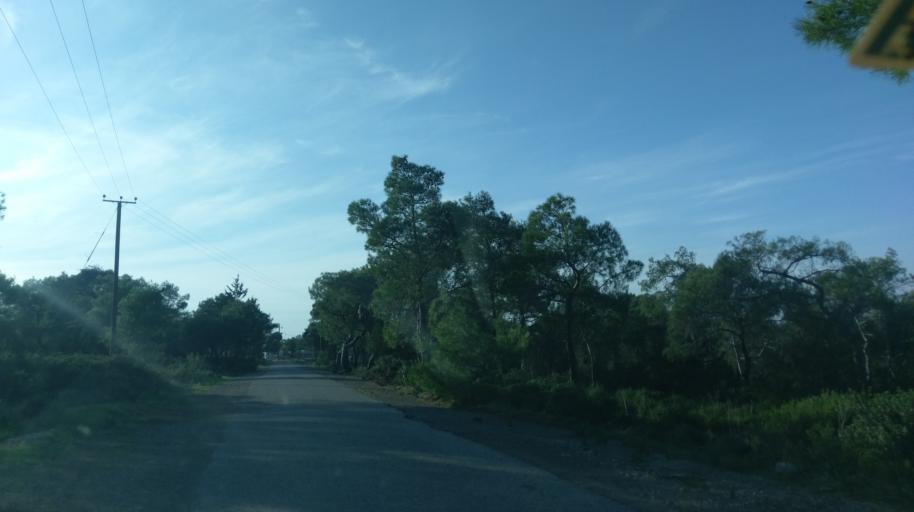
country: CY
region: Ammochostos
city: Lefkonoiko
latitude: 35.3332
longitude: 33.5887
